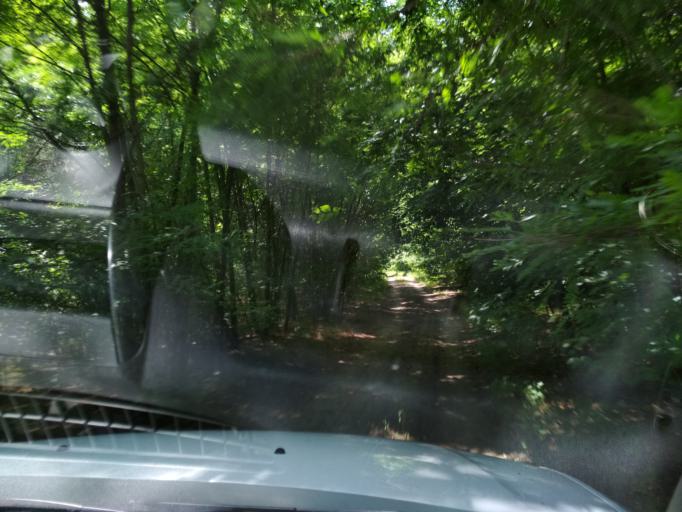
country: HU
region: Pest
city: Tapiosag
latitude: 47.4078
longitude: 19.6445
